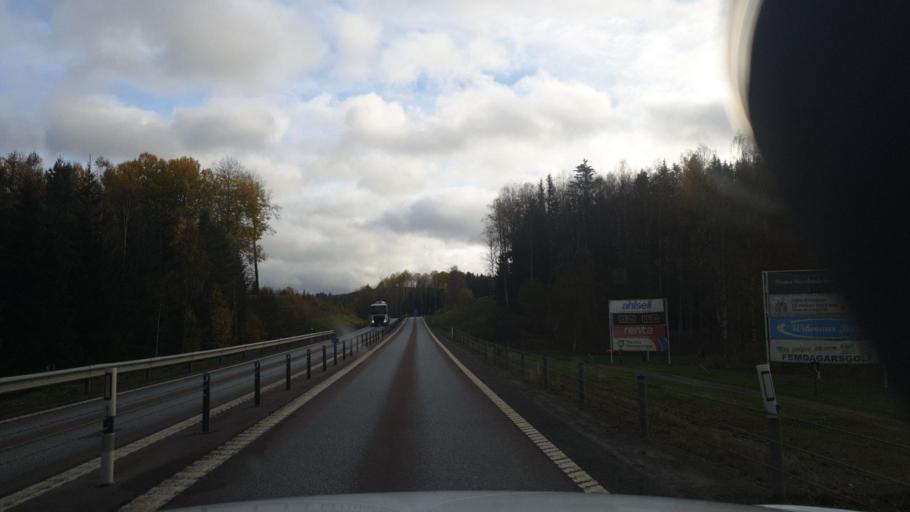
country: SE
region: Vaermland
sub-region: Arvika Kommun
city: Arvika
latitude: 59.6600
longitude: 12.7773
